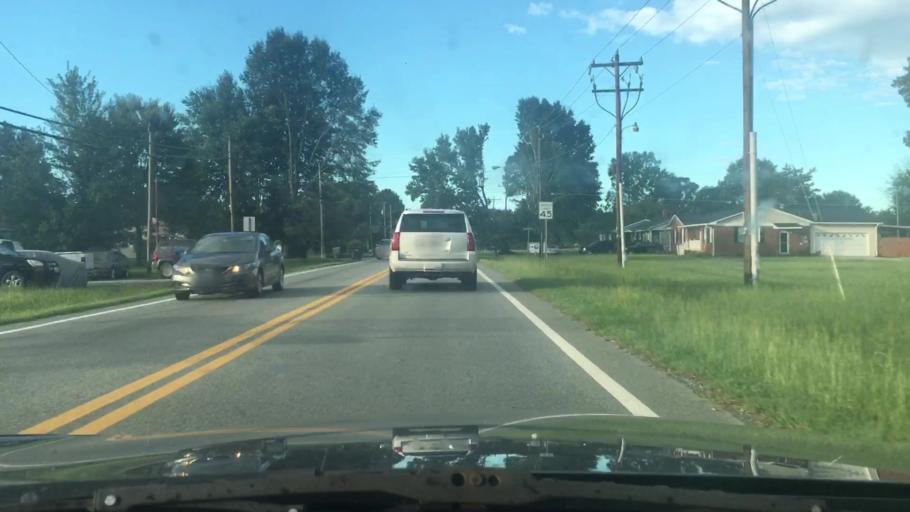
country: US
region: North Carolina
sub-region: Alamance County
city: Green Level
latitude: 36.1227
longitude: -79.3494
